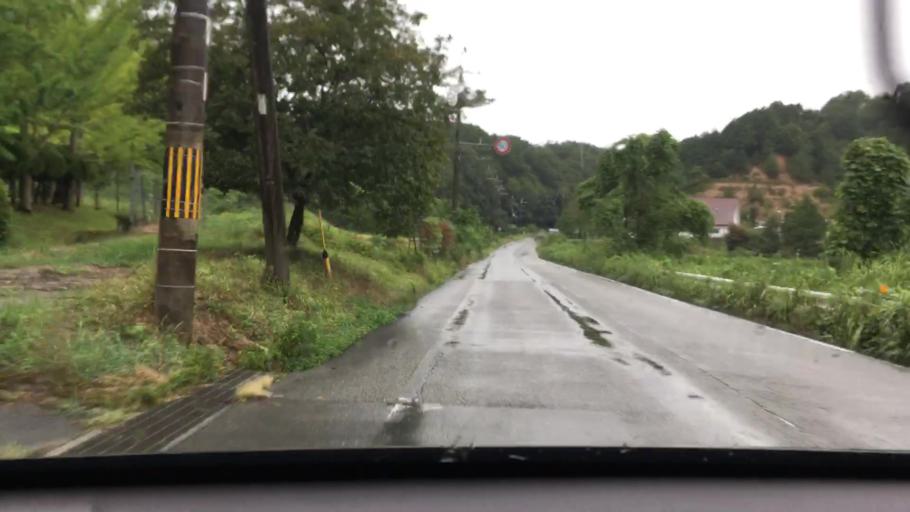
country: JP
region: Hyogo
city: Toyooka
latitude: 35.3083
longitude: 134.8719
